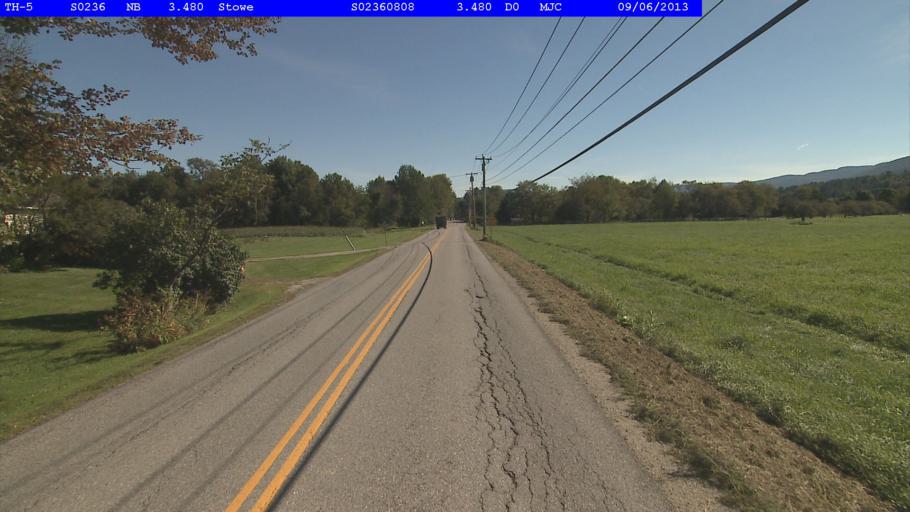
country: US
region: Vermont
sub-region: Lamoille County
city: Morristown
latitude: 44.4725
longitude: -72.7230
